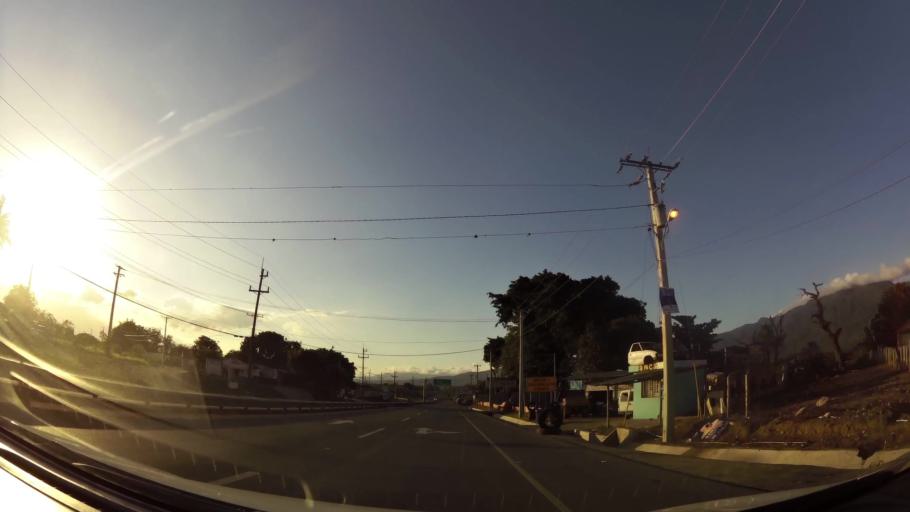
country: DO
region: Santiago
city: Palmar Arriba
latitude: 19.5141
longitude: -70.7605
